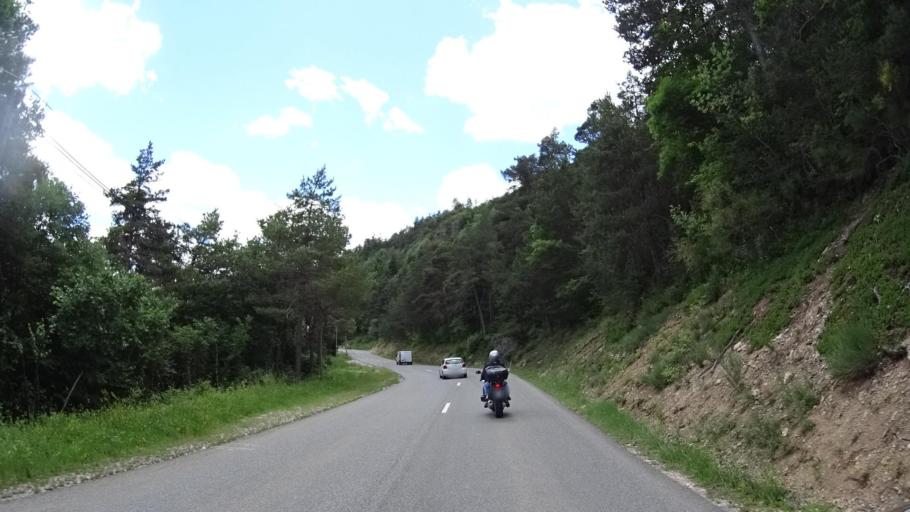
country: FR
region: Provence-Alpes-Cote d'Azur
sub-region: Departement des Alpes-de-Haute-Provence
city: Annot
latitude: 44.0196
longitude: 6.5560
